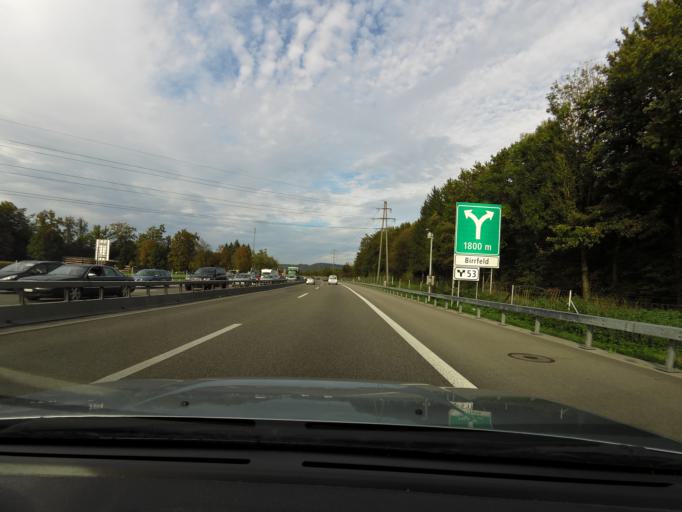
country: CH
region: Aargau
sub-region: Bezirk Brugg
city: Birr
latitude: 47.4274
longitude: 8.2359
